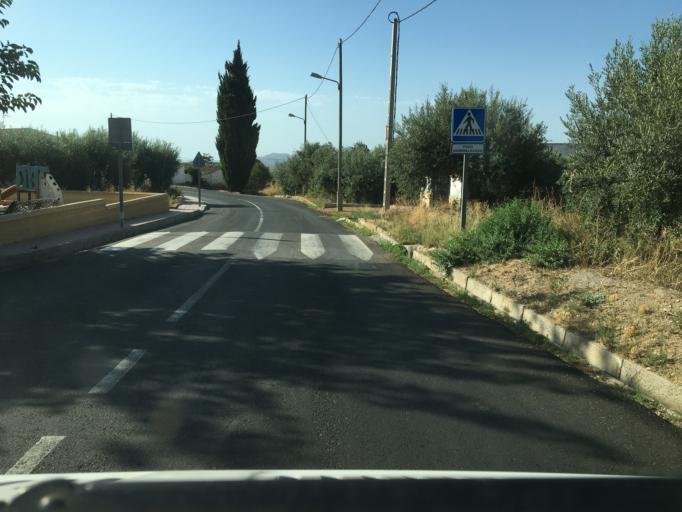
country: ES
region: Andalusia
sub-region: Provincia de Almeria
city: Huercal-Overa
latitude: 37.4699
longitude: -1.8935
